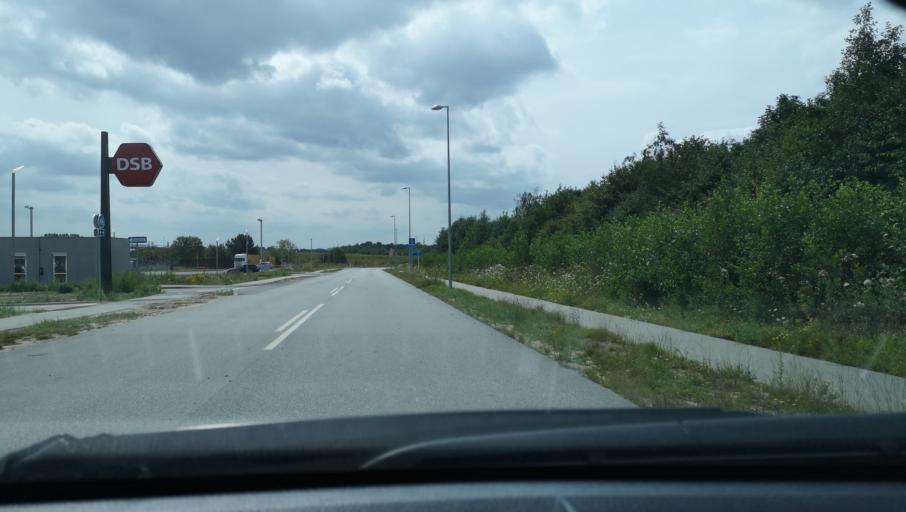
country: DK
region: Zealand
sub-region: Solrod Kommune
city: Solrod
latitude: 55.5003
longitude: 12.1706
